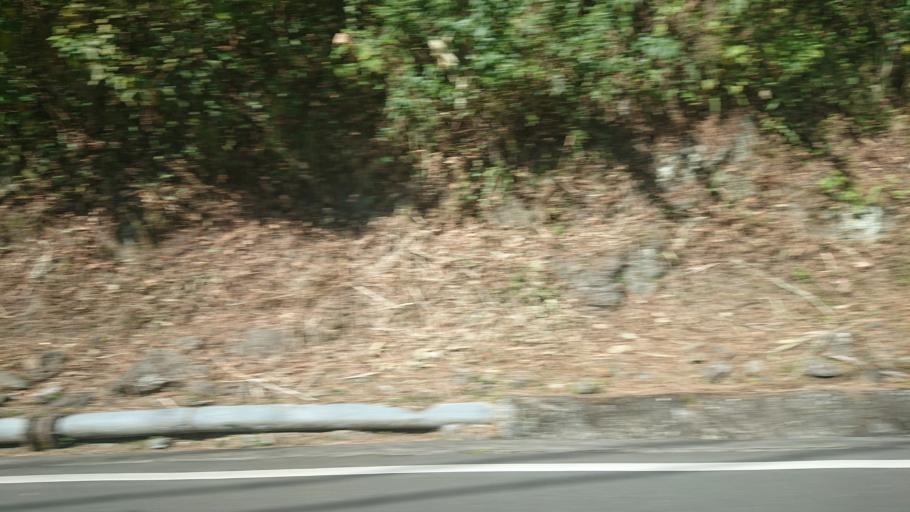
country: TW
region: Taiwan
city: Lugu
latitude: 23.4681
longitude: 120.7304
